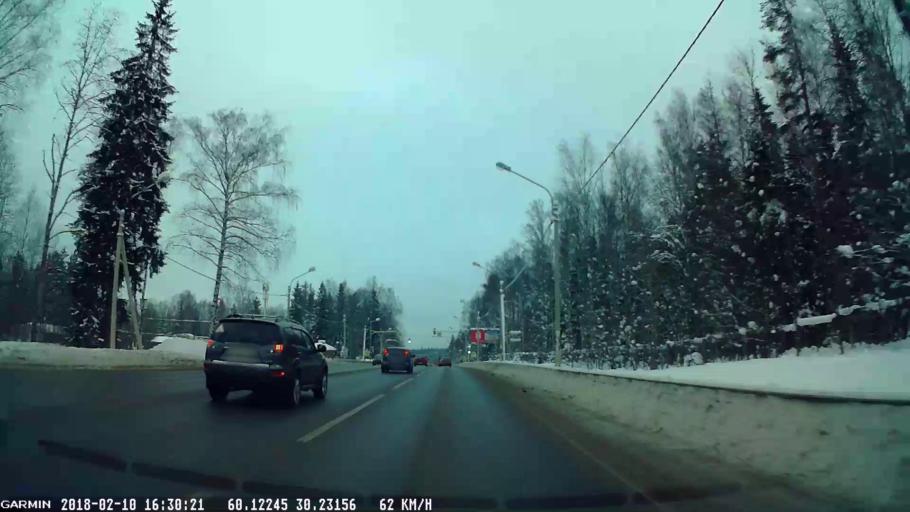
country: RU
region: St.-Petersburg
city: Levashovo
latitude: 60.1231
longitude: 30.2309
